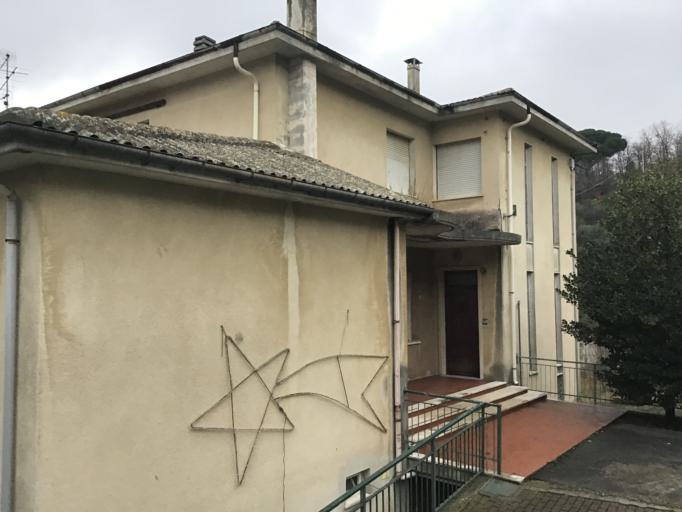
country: IT
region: Liguria
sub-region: Provincia di Savona
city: Orco Feglino
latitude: 44.2227
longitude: 8.3442
